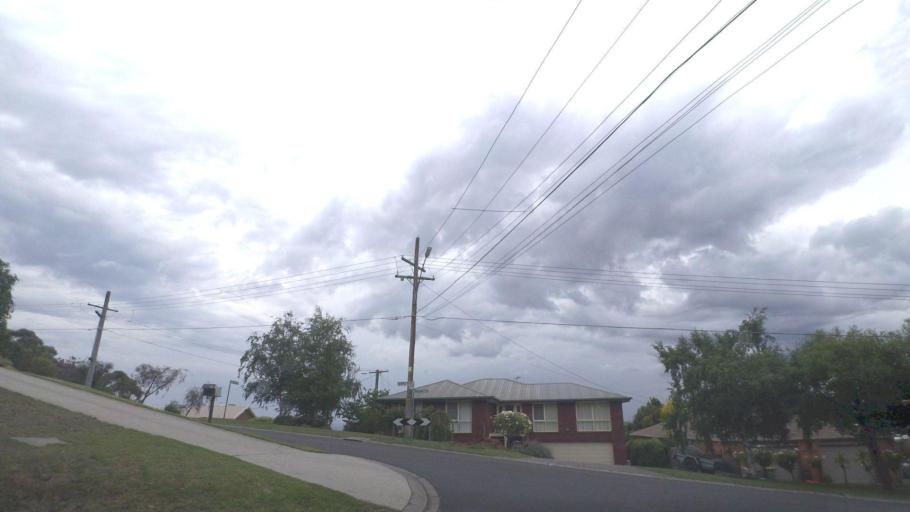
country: AU
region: Victoria
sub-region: Yarra Ranges
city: Lilydale
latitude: -37.7612
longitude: 145.3690
